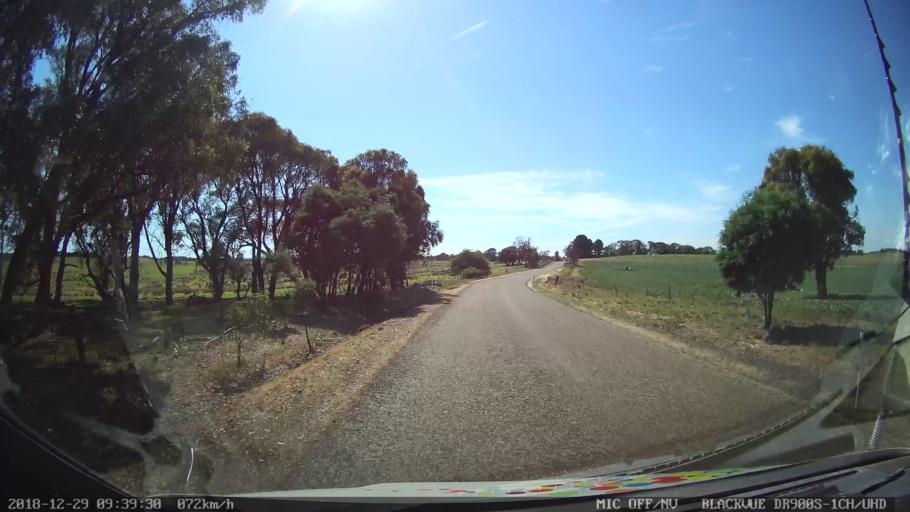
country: AU
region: New South Wales
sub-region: Upper Lachlan Shire
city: Crookwell
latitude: -34.6541
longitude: 149.3861
